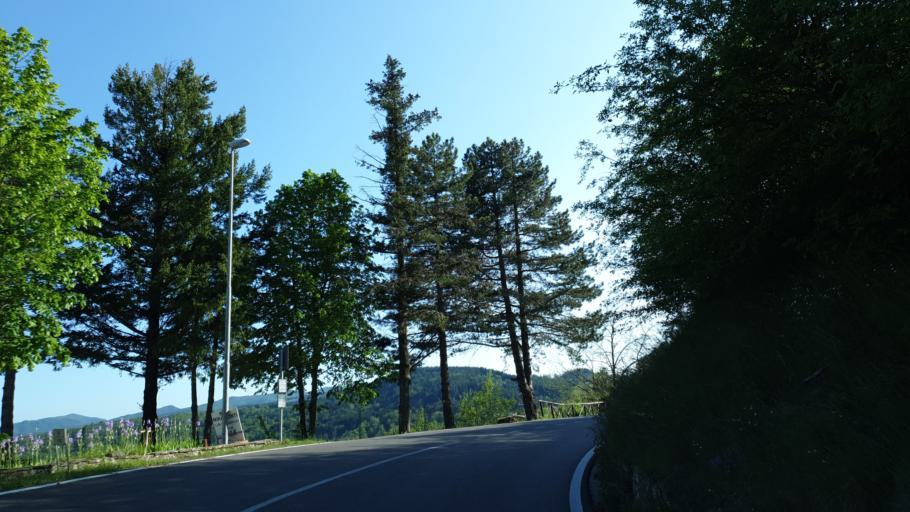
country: IT
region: Tuscany
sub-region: Province of Arezzo
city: Montemignaio
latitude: 43.7847
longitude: 11.6039
